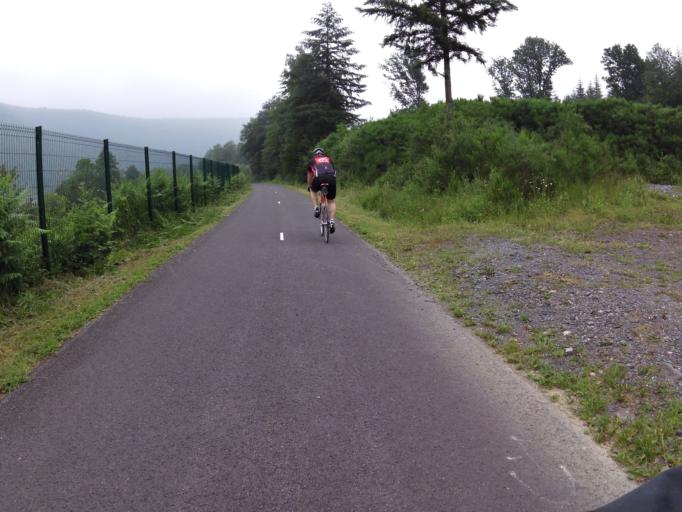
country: FR
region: Champagne-Ardenne
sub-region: Departement des Ardennes
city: Revin
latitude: 49.9678
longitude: 4.6645
